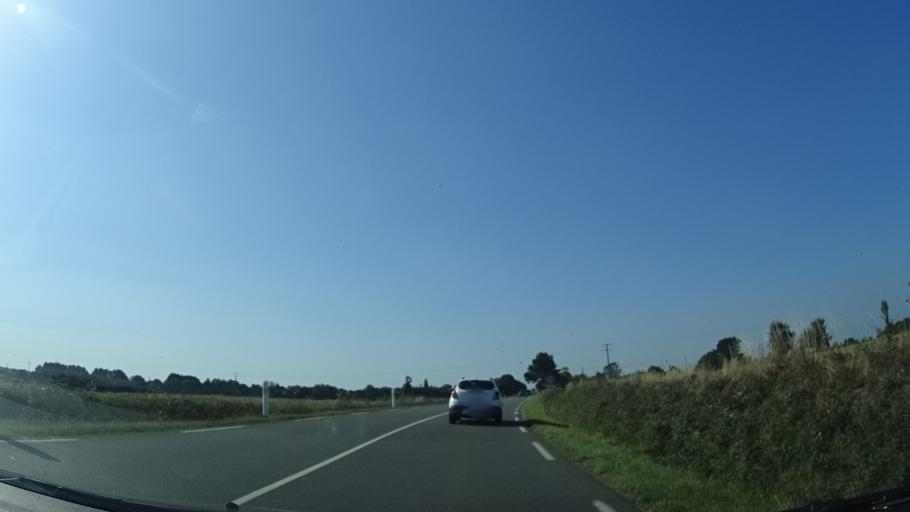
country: FR
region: Brittany
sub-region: Departement du Finistere
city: Plonevez-Porzay
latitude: 48.1053
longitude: -4.2461
